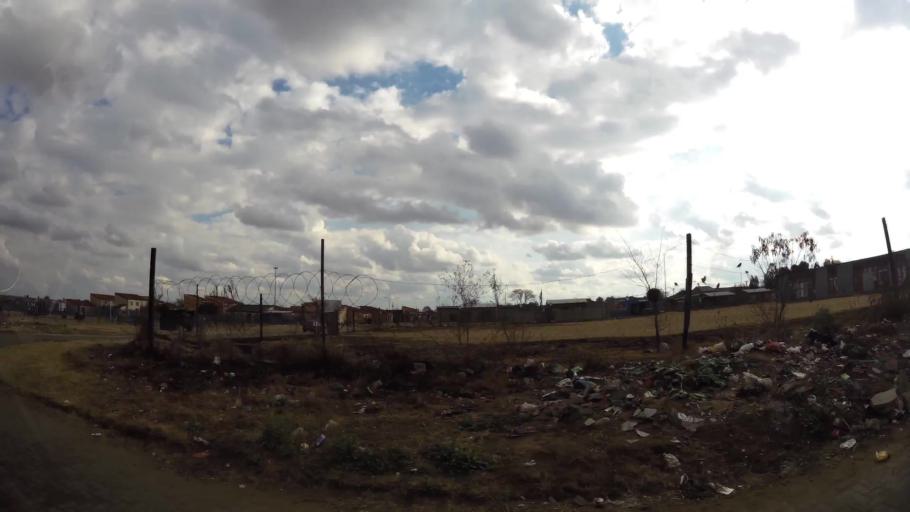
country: ZA
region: Orange Free State
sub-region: Fezile Dabi District Municipality
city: Sasolburg
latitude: -26.8418
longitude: 27.8437
